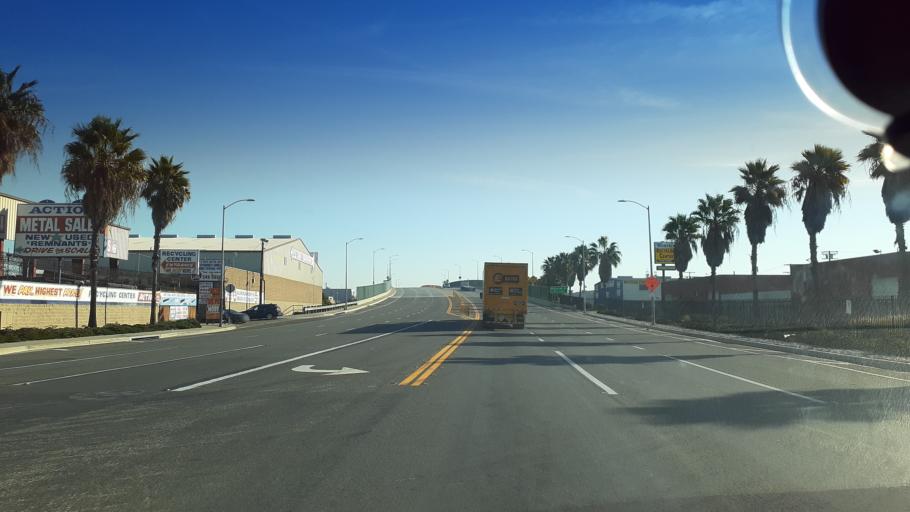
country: US
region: California
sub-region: Los Angeles County
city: Carson
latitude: 33.7911
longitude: -118.2441
